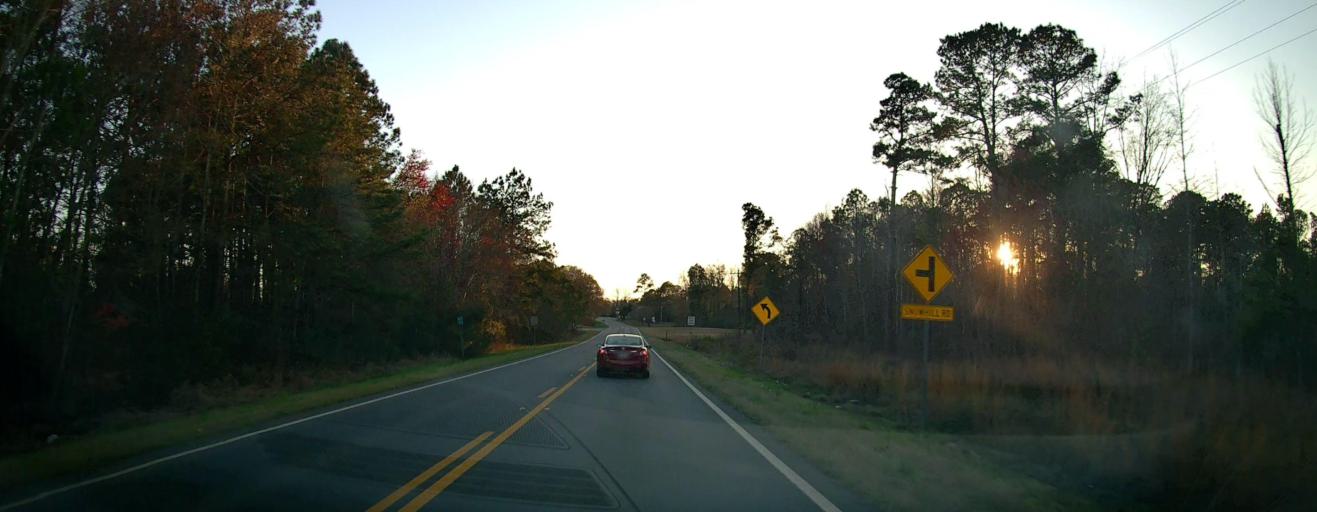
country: US
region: Georgia
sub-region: Dodge County
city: Chester
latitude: 32.3486
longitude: -83.0336
